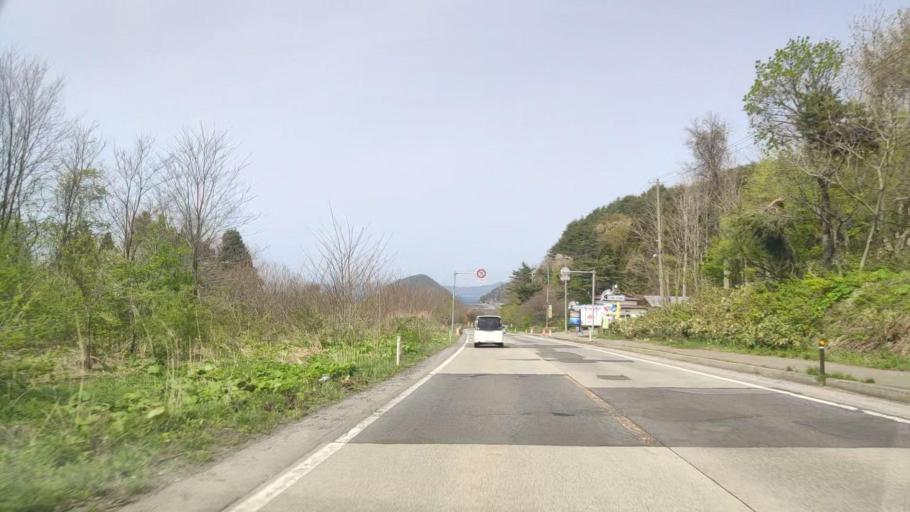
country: JP
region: Aomori
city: Aomori Shi
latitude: 40.8631
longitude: 140.8451
